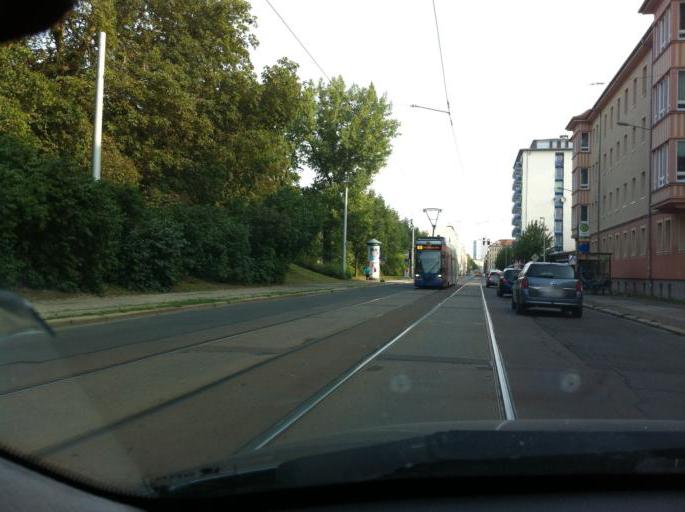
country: DE
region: Saxony
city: Leipzig
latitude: 51.3166
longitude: 12.3784
